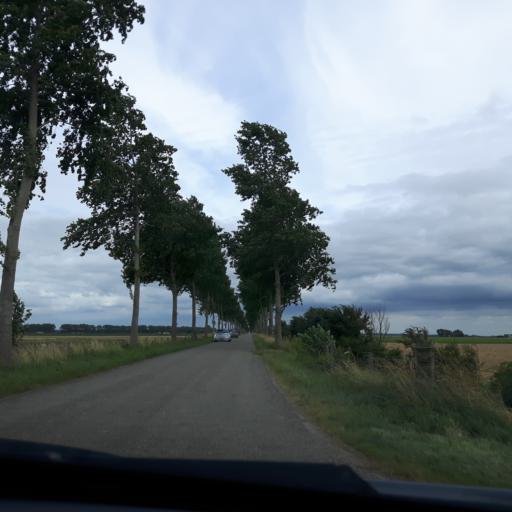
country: NL
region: Zeeland
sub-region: Gemeente Noord-Beveland
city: Kamperland
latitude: 51.5637
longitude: 3.7130
